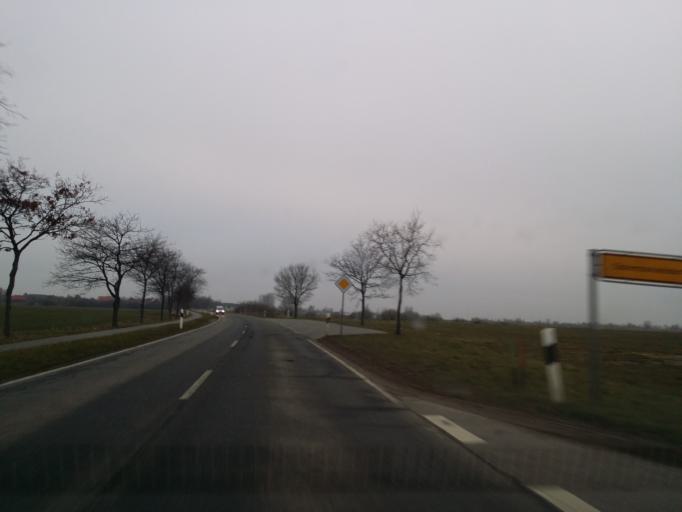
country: DE
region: Schleswig-Holstein
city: Fehmarn
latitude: 54.4467
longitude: 11.1642
